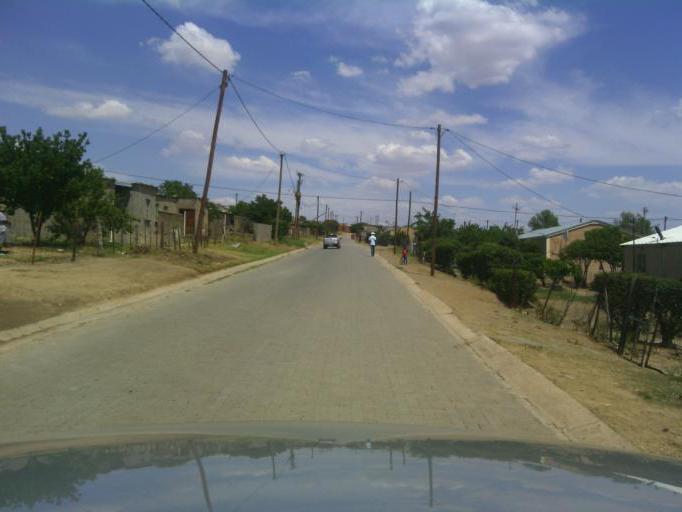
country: ZA
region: Orange Free State
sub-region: Xhariep District Municipality
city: Dewetsdorp
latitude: -29.5848
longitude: 26.6803
